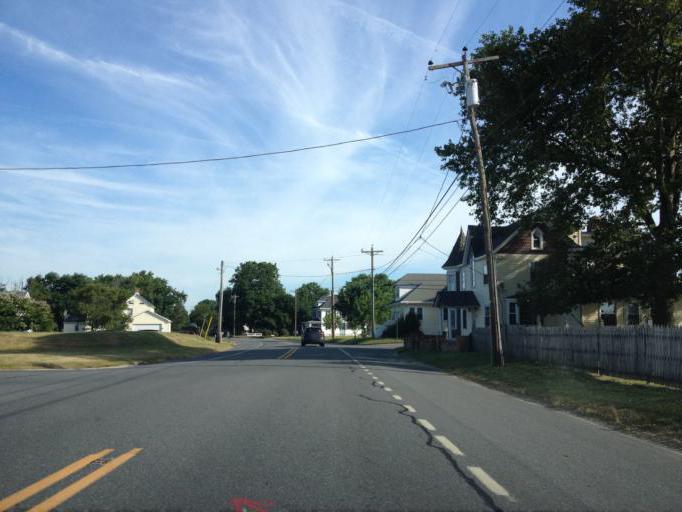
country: US
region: Delaware
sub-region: Sussex County
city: Selbyville
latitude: 38.4934
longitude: -75.1673
